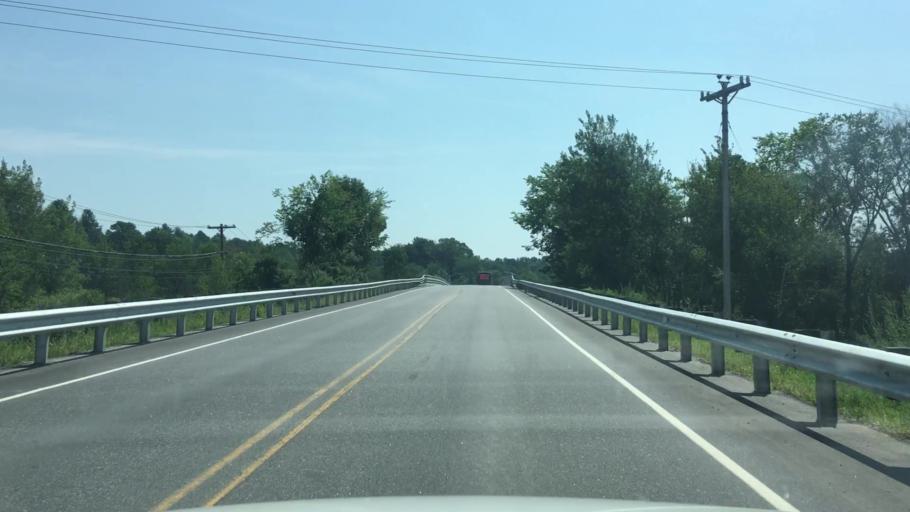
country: US
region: Maine
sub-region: Kennebec County
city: Hallowell
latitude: 44.2978
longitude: -69.8088
